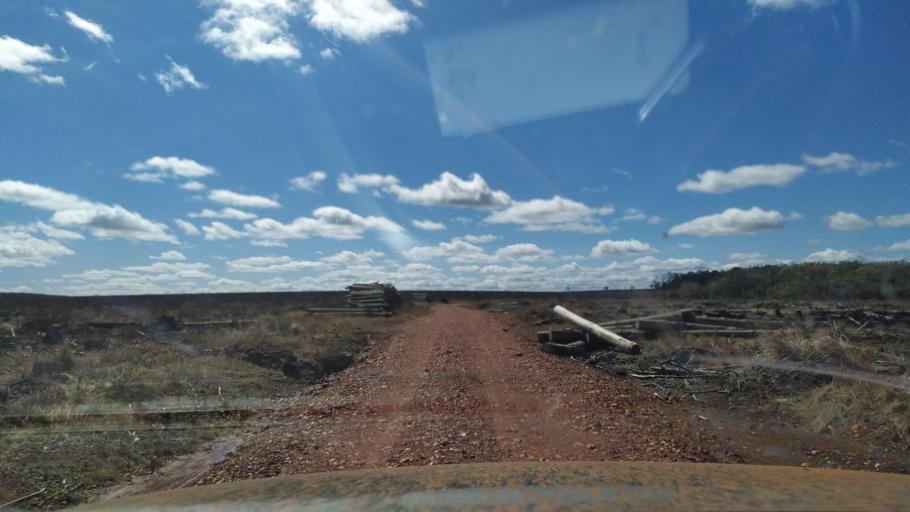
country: AR
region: Corrientes
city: Gobernador Ingeniero Valentin Virasoro
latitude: -28.2928
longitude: -56.0525
